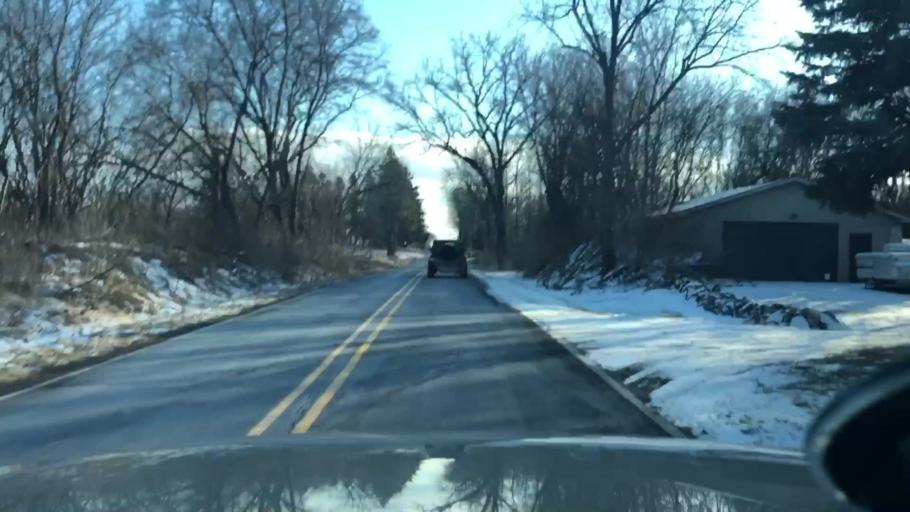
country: US
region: Michigan
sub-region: Jackson County
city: Vandercook Lake
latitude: 42.1234
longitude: -84.4515
